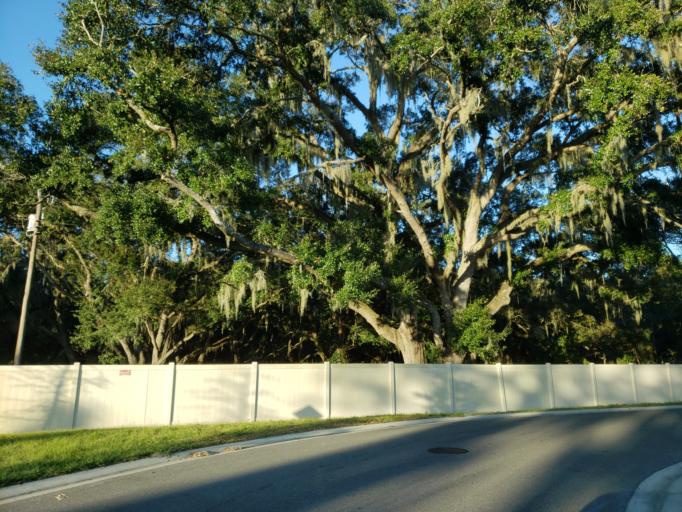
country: US
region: Florida
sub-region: Hillsborough County
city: Boyette
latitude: 27.8243
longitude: -82.2469
